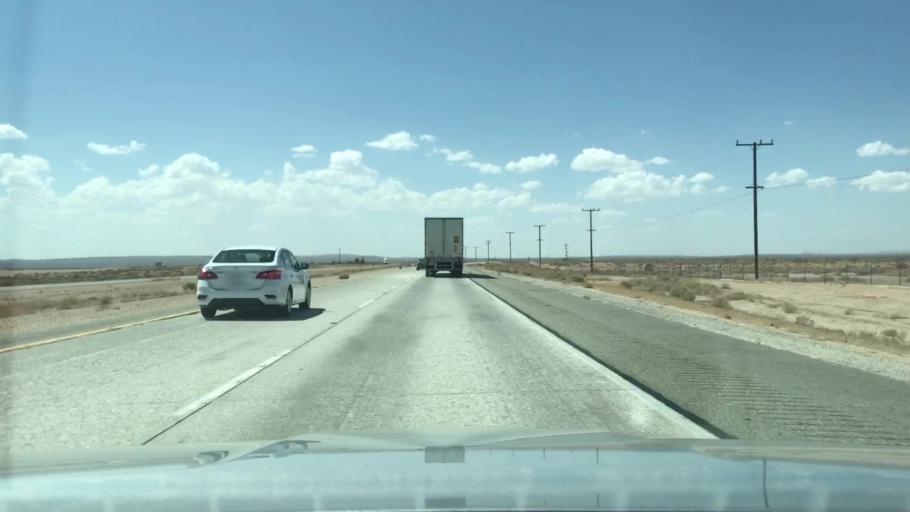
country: US
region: California
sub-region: San Bernardino County
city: Lenwood
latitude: 34.9236
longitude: -117.3009
